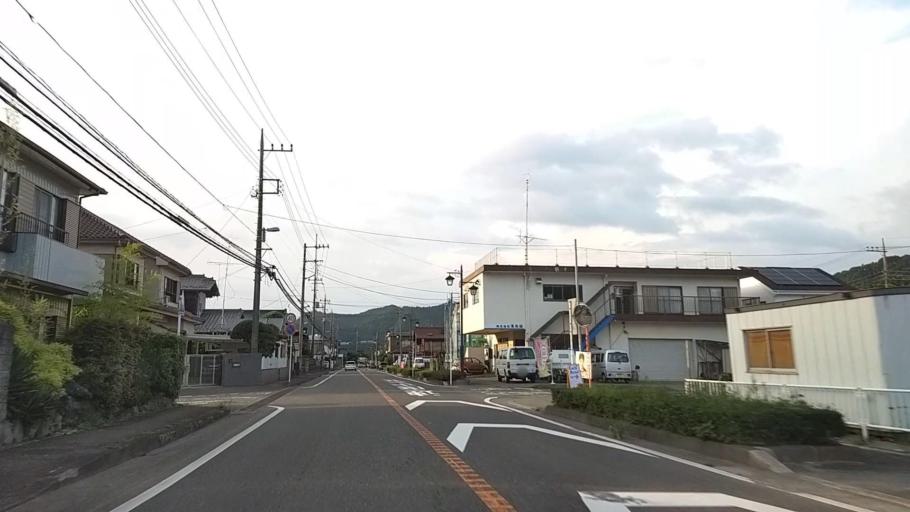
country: JP
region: Kanagawa
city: Hadano
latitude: 35.5198
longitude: 139.2314
